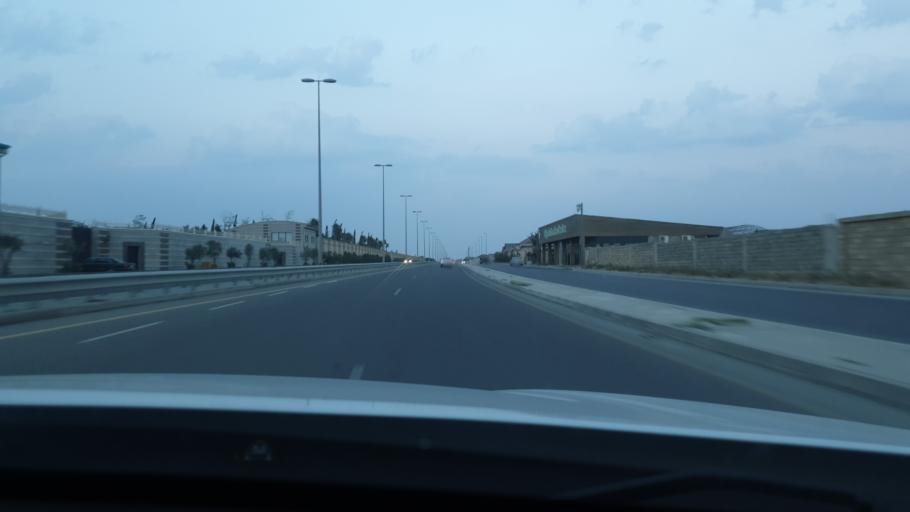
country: AZ
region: Baki
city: Nardaran
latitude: 40.5830
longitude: 50.0131
